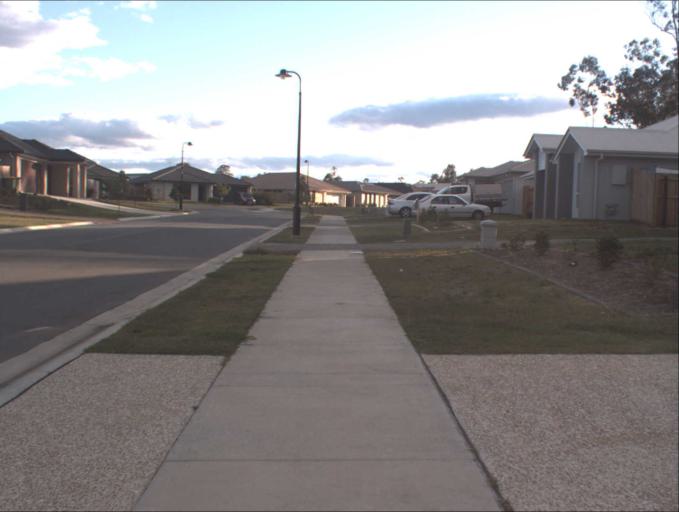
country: AU
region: Queensland
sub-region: Logan
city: North Maclean
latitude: -27.8023
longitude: 152.9596
